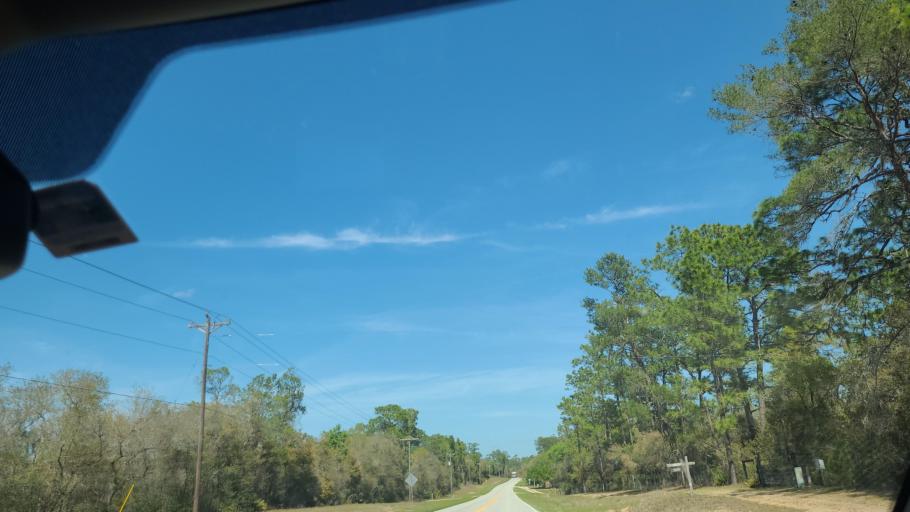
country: US
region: Florida
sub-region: Putnam County
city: Interlachen
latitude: 29.3680
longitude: -81.8068
